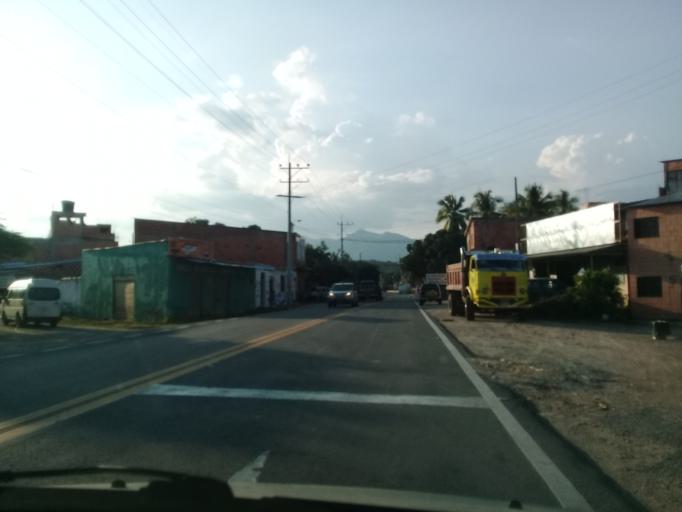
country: CO
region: Cundinamarca
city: Tocaima
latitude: 4.4546
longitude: -74.6426
